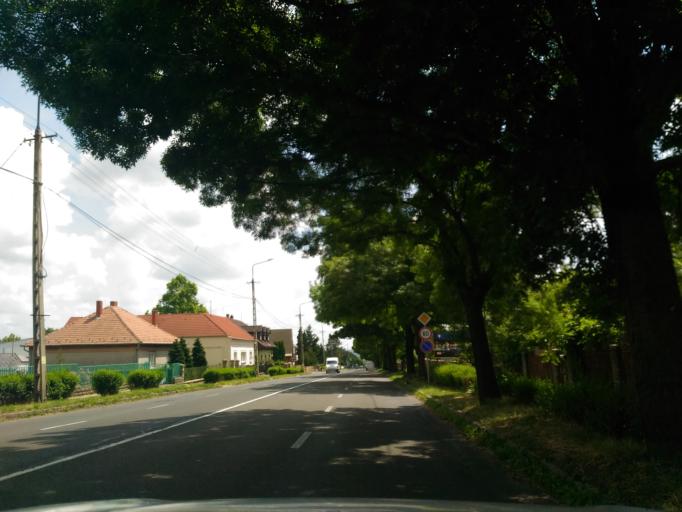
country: HU
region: Baranya
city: Pecs
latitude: 46.1066
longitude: 18.2637
